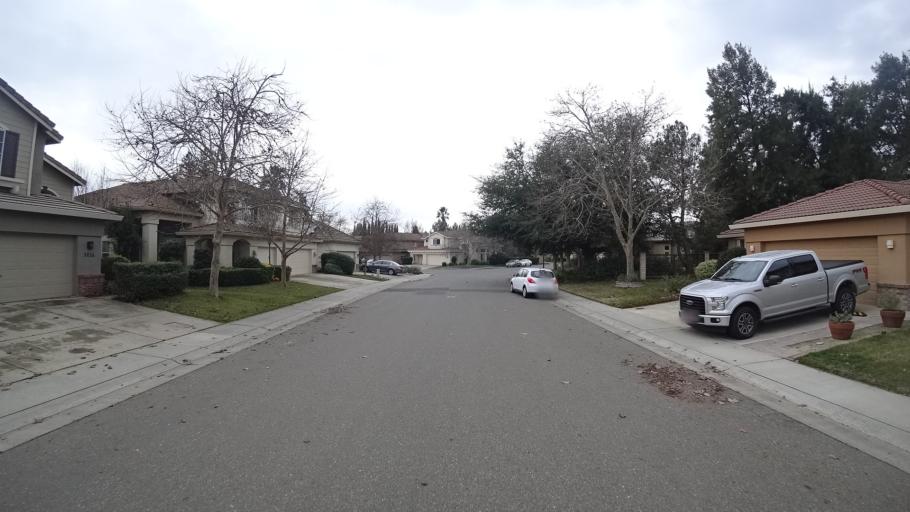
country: US
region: California
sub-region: Yolo County
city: Davis
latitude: 38.5552
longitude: -121.7120
